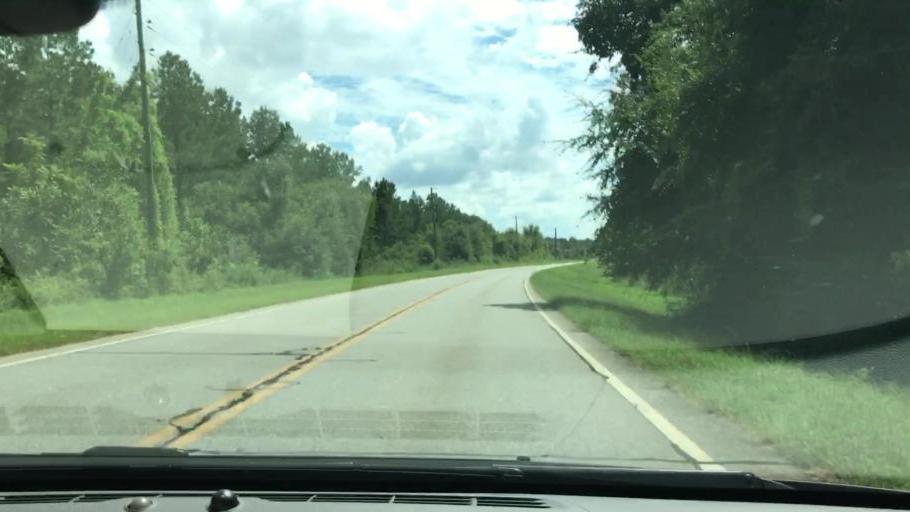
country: US
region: Georgia
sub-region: Quitman County
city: Georgetown
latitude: 32.0773
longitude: -85.0388
